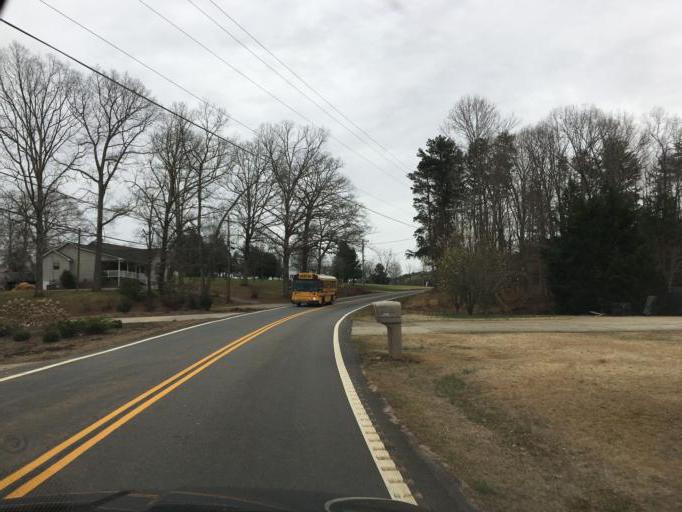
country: US
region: South Carolina
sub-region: Greenville County
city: Berea
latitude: 34.9256
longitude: -82.4870
